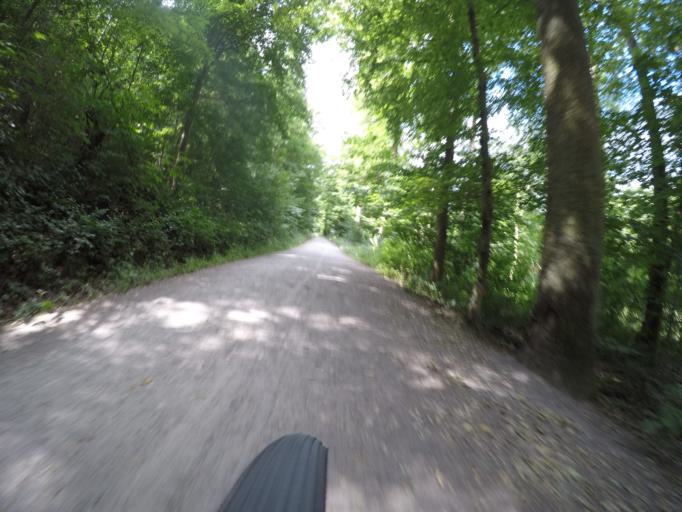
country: DE
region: Baden-Wuerttemberg
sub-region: Regierungsbezirk Stuttgart
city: Stuttgart Feuerbach
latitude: 48.7898
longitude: 9.1432
